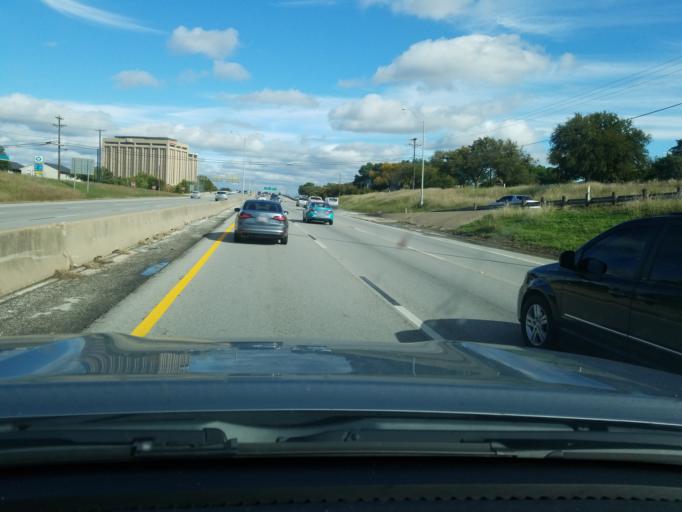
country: US
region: Texas
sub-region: Tarrant County
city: Westworth
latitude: 32.7345
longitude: -97.4230
